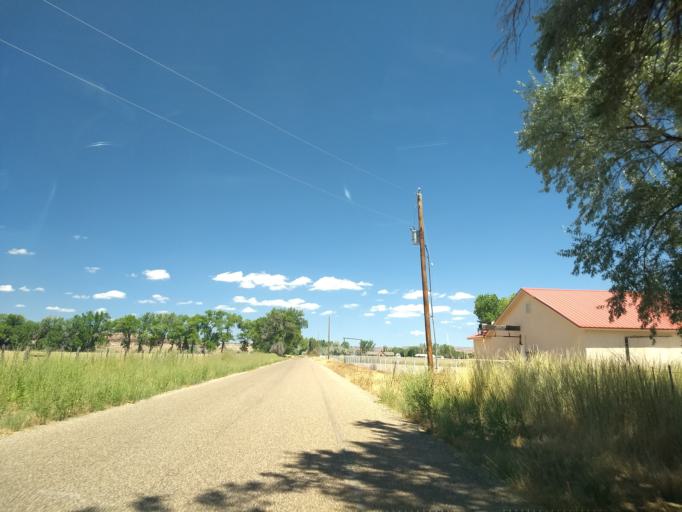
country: US
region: Arizona
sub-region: Coconino County
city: Fredonia
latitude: 36.9362
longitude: -112.5353
